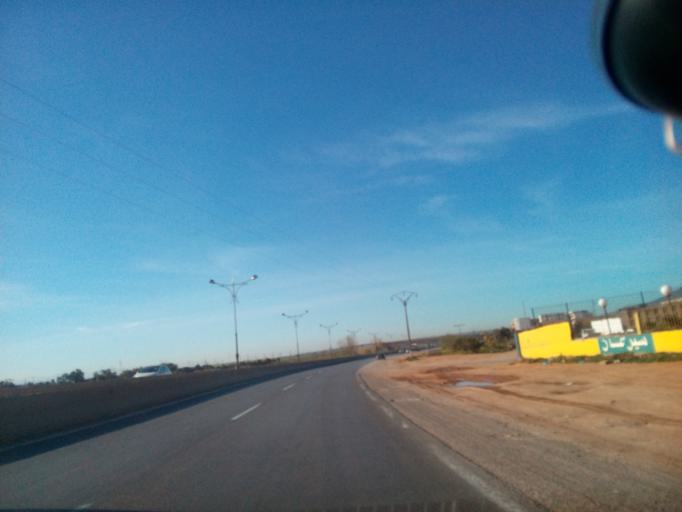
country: DZ
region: Oran
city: Ain el Bya
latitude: 35.7789
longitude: -0.4149
